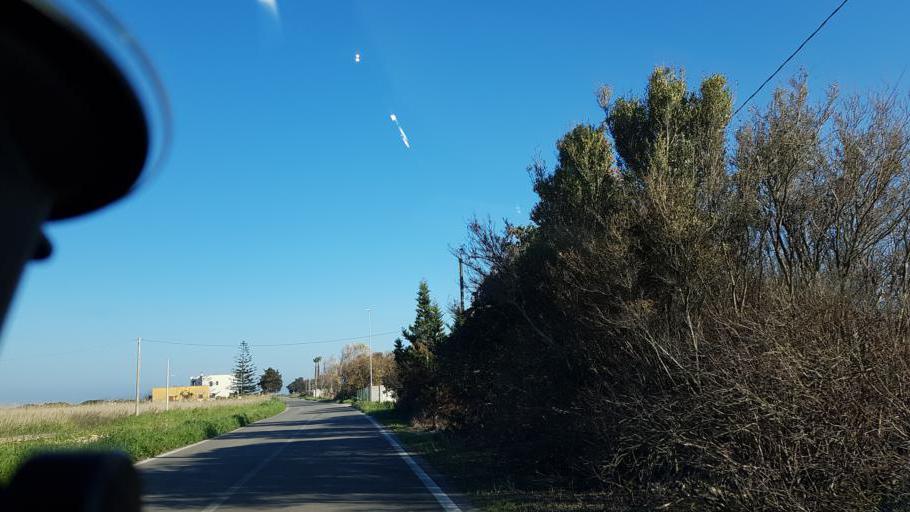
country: IT
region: Apulia
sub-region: Provincia di Lecce
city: Giorgilorio
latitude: 40.4508
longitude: 18.2221
